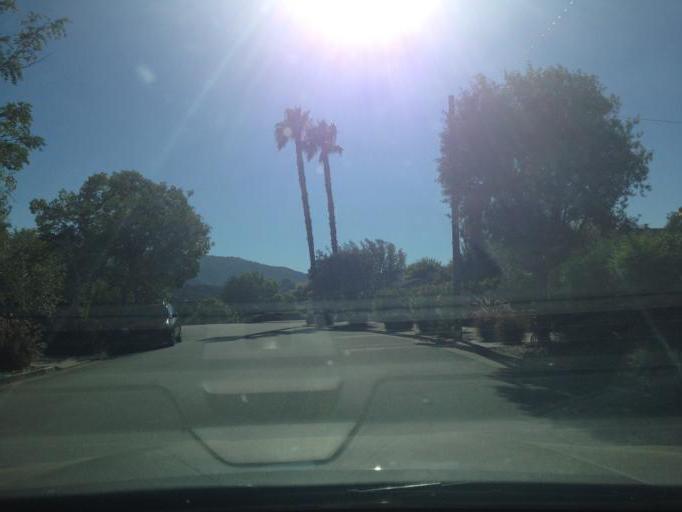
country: US
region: California
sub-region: Santa Clara County
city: Cambrian Park
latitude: 37.2149
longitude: -121.8675
